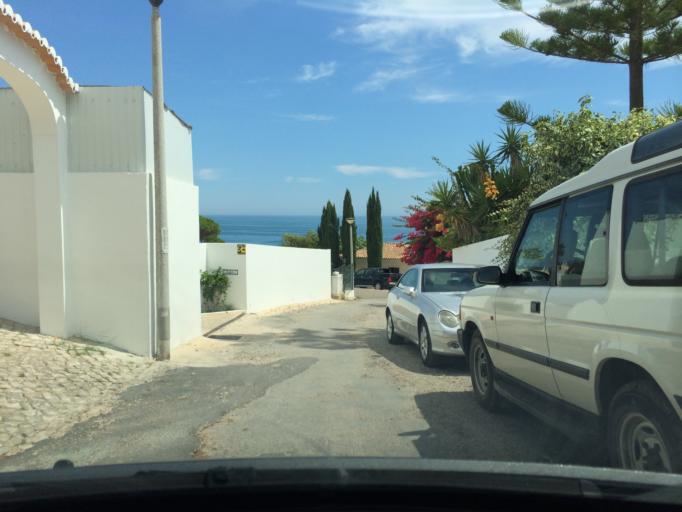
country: PT
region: Faro
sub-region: Albufeira
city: Albufeira
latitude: 37.0908
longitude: -8.1929
